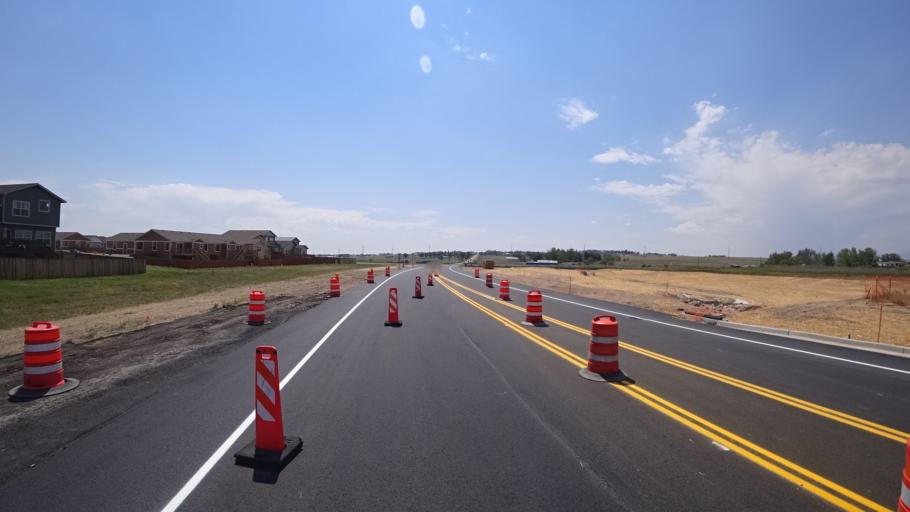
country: US
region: Colorado
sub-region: El Paso County
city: Cimarron Hills
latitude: 38.9277
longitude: -104.6078
